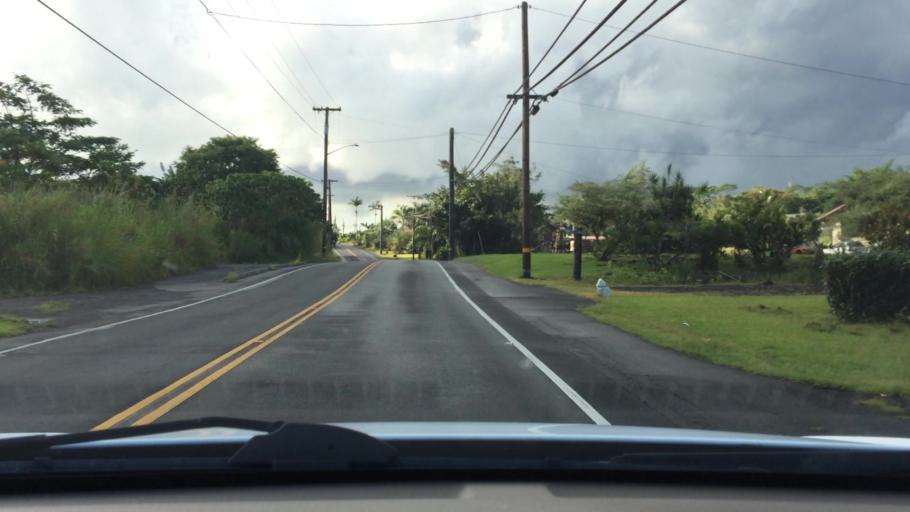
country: US
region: Hawaii
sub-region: Hawaii County
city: Hawaiian Paradise Park
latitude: 19.4975
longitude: -154.9523
